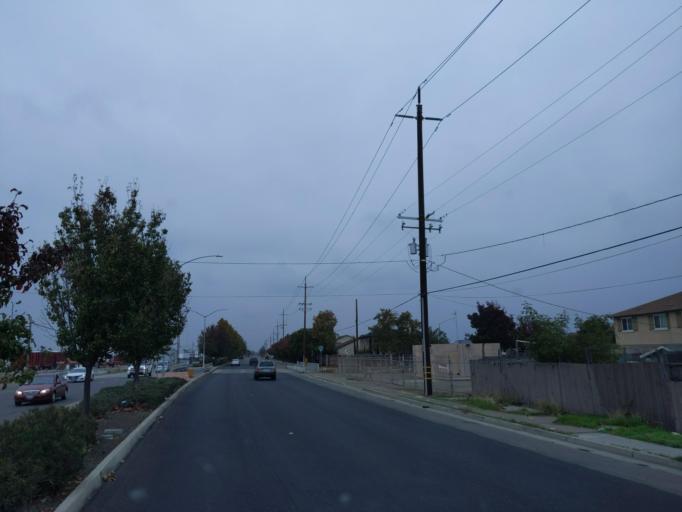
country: US
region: California
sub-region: San Joaquin County
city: Kennedy
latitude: 37.9227
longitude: -121.2636
